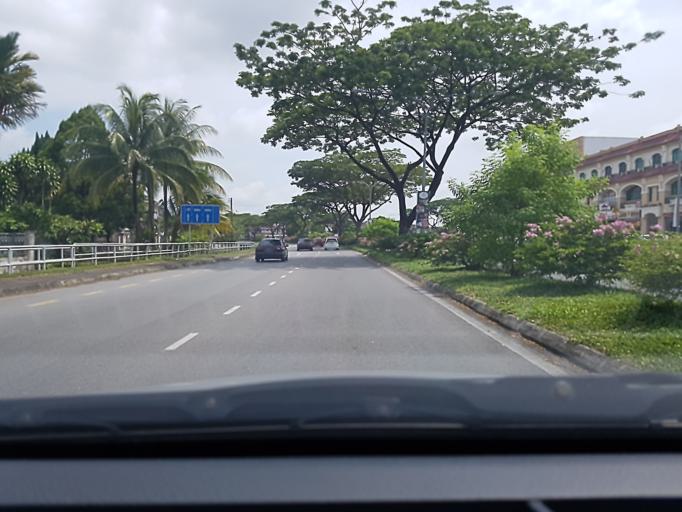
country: MY
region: Sarawak
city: Kuching
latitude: 1.5167
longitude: 110.3666
